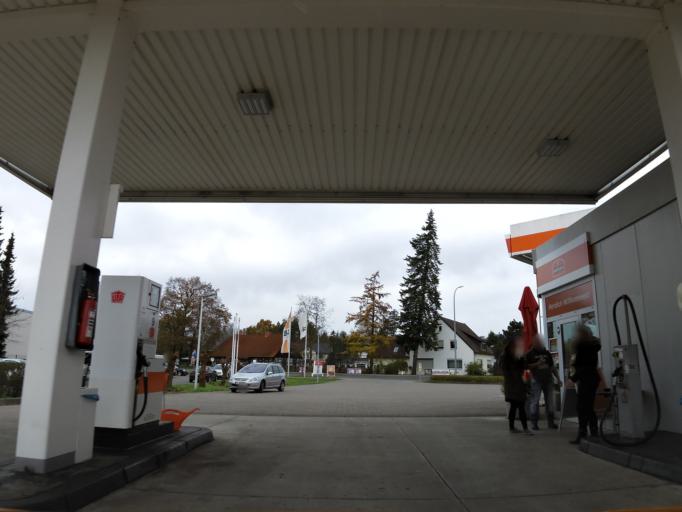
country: DE
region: Lower Saxony
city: Wietze
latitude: 52.6570
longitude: 9.8275
